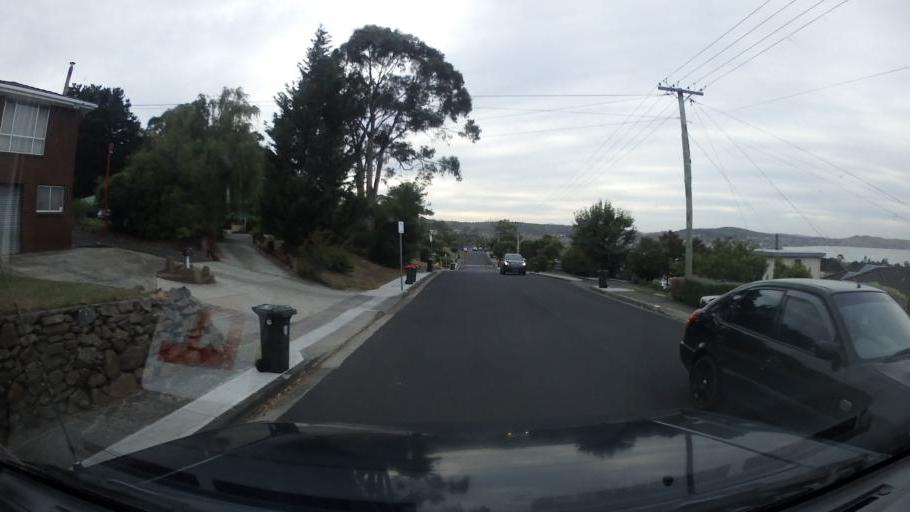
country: AU
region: Tasmania
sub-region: Clarence
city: Bellerive
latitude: -42.8715
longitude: 147.3798
